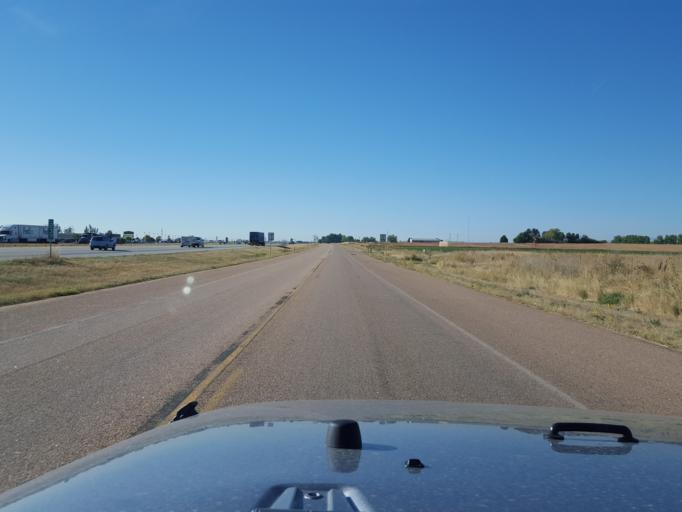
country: US
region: Colorado
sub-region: Weld County
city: Firestone
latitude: 40.1158
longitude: -104.9806
